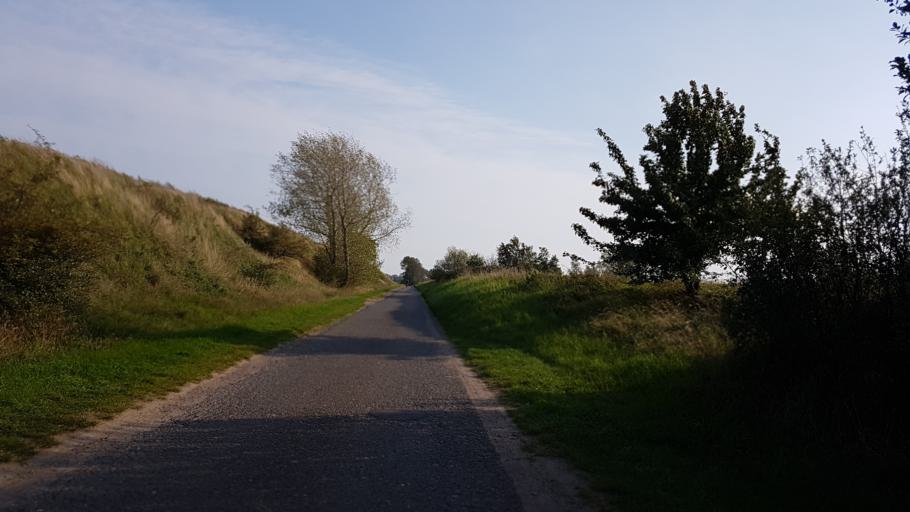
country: DE
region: Mecklenburg-Vorpommern
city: Sagard
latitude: 54.5378
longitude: 13.5103
